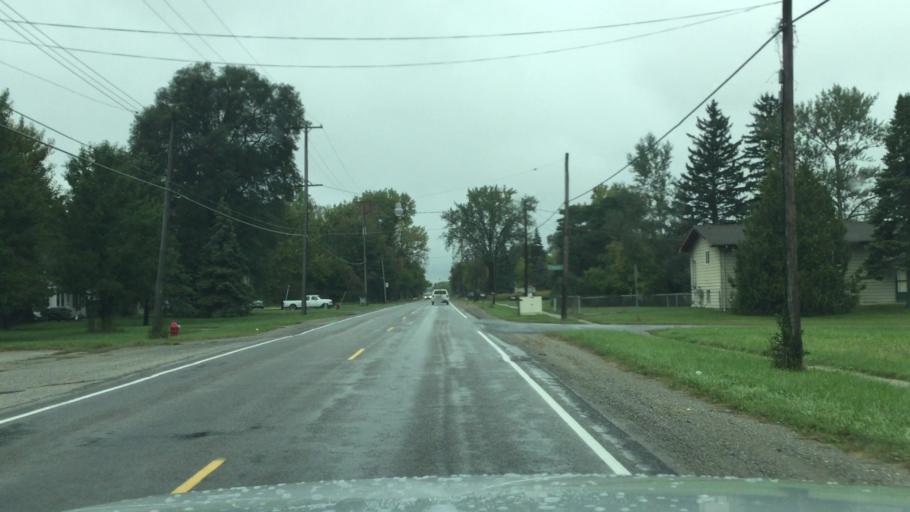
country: US
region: Michigan
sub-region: Saginaw County
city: Carrollton
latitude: 43.4735
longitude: -83.9458
